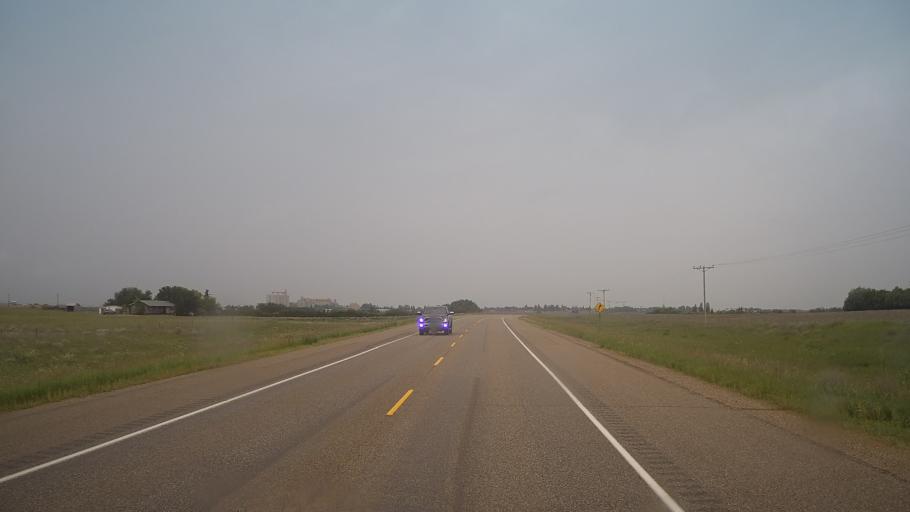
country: CA
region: Saskatchewan
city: Biggar
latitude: 52.0563
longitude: -107.9436
